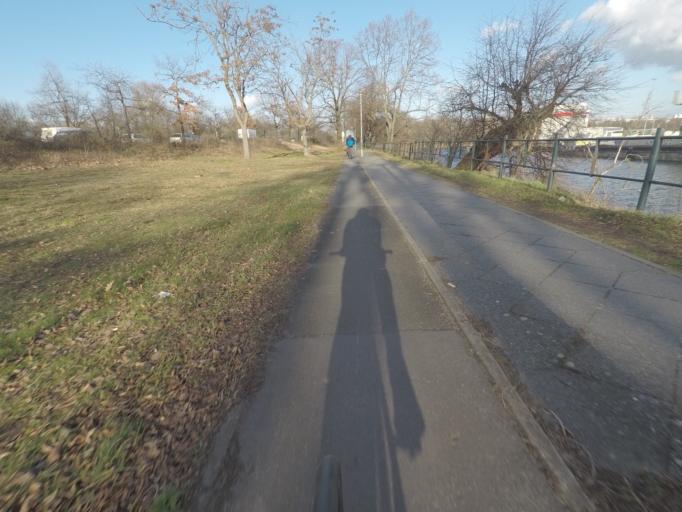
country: DE
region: Berlin
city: Moabit
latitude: 52.5394
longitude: 13.3312
